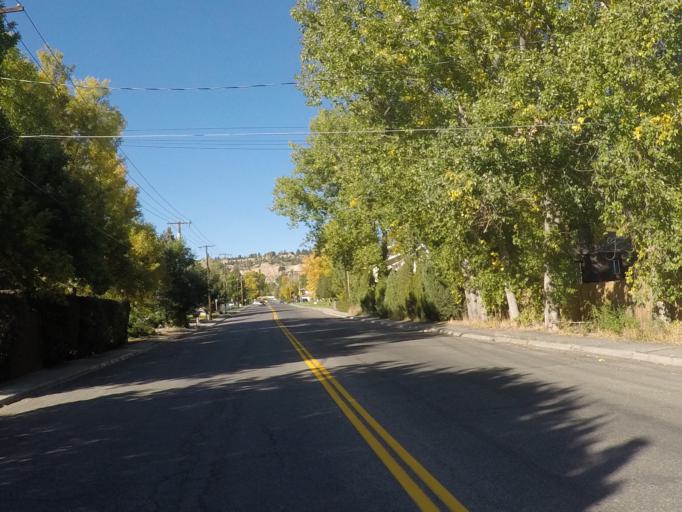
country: US
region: Montana
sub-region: Yellowstone County
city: Billings
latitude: 45.7929
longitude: -108.5904
